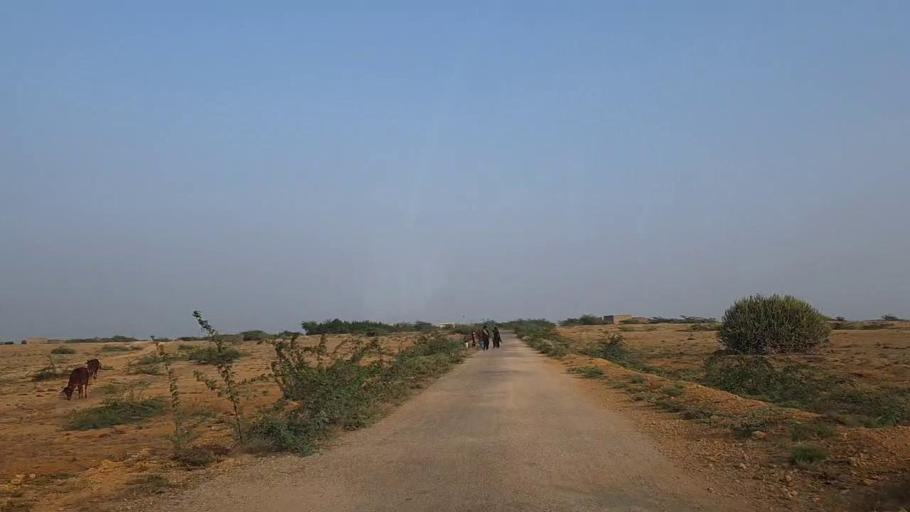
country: PK
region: Sindh
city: Thatta
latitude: 24.6901
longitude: 67.8236
